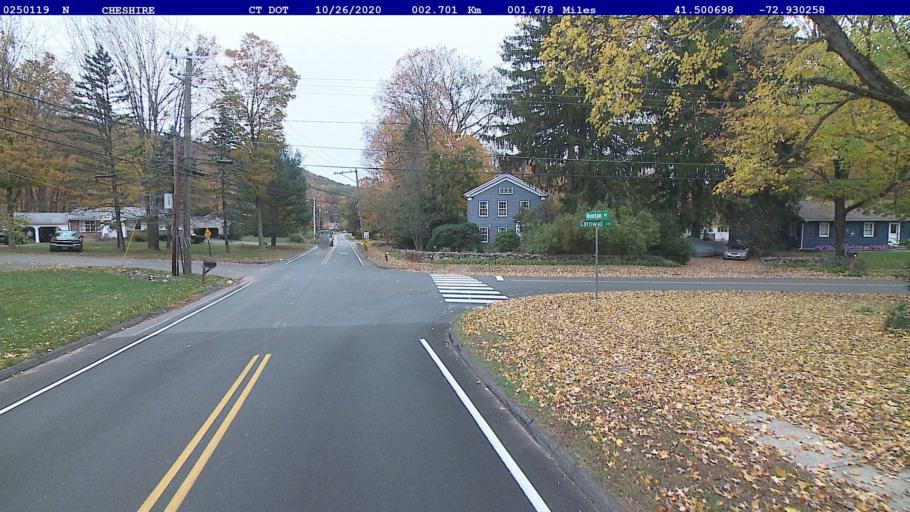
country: US
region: Connecticut
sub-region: New Haven County
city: Cheshire
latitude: 41.5007
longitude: -72.9302
